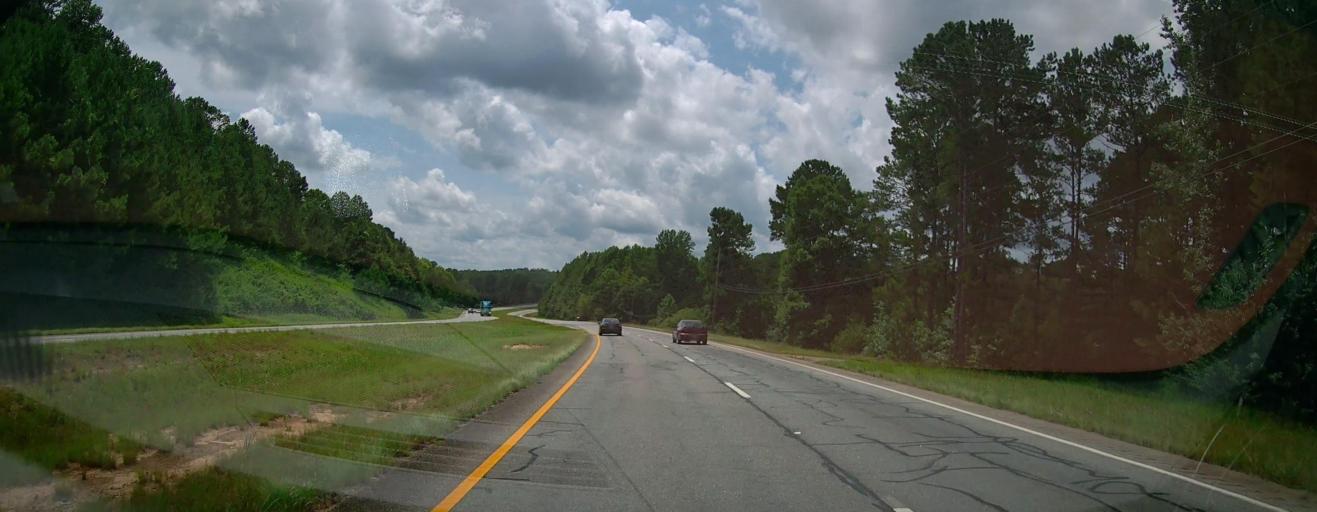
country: US
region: Georgia
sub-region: Heard County
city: Franklin
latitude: 33.2576
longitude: -85.0552
